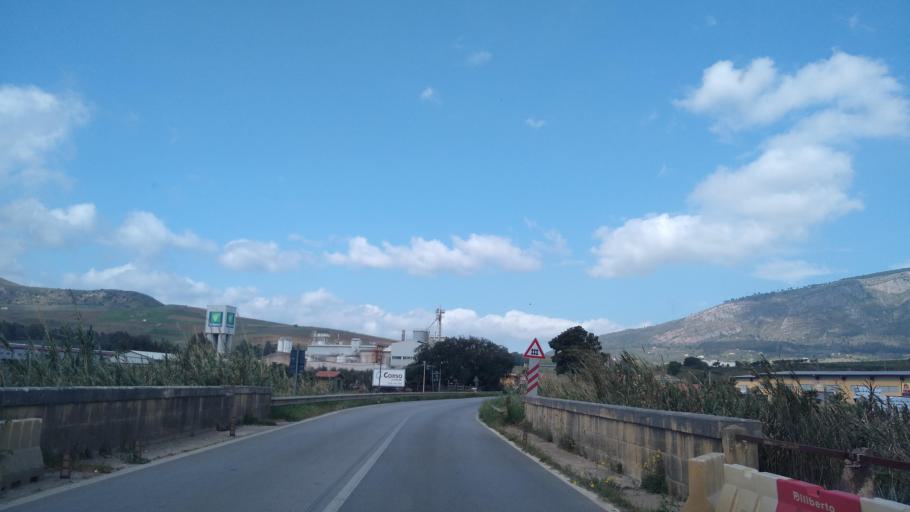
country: IT
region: Sicily
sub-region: Trapani
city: Alcamo
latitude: 37.9678
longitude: 12.9181
